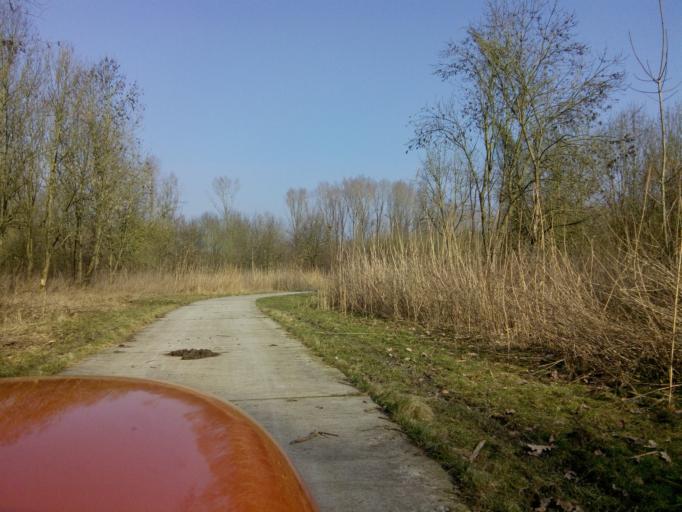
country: NL
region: Gelderland
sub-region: Gemeente Nijkerk
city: Nijkerk
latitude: 52.2830
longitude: 5.4635
